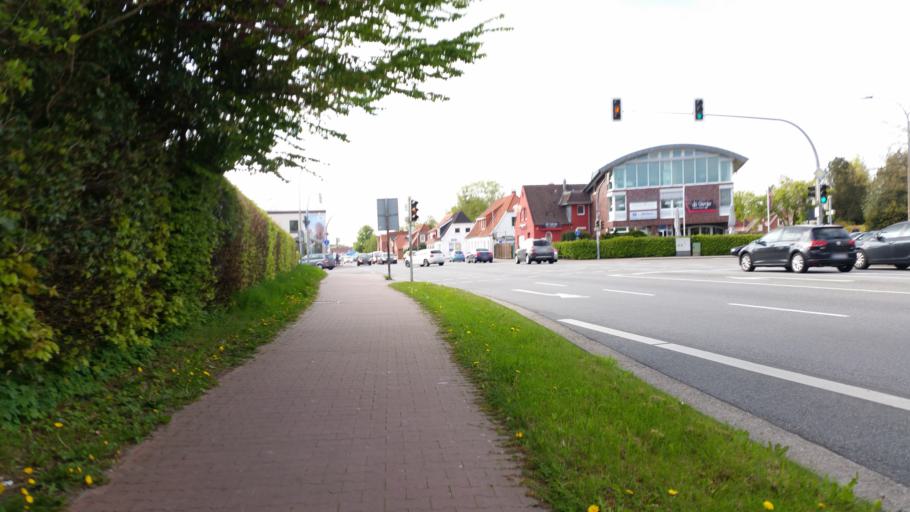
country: DE
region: Lower Saxony
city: Aurich
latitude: 53.4614
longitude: 7.4912
